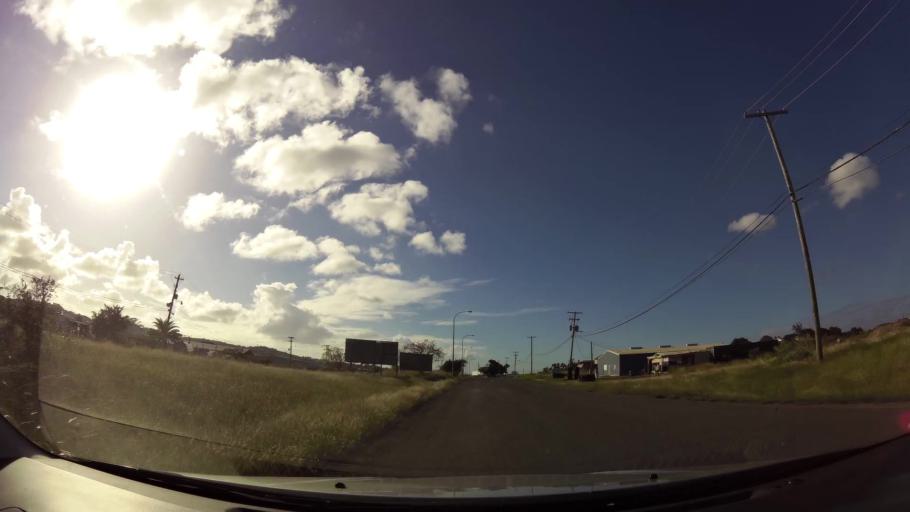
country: AG
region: Saint George
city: Piggotts
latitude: 17.1155
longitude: -61.8054
